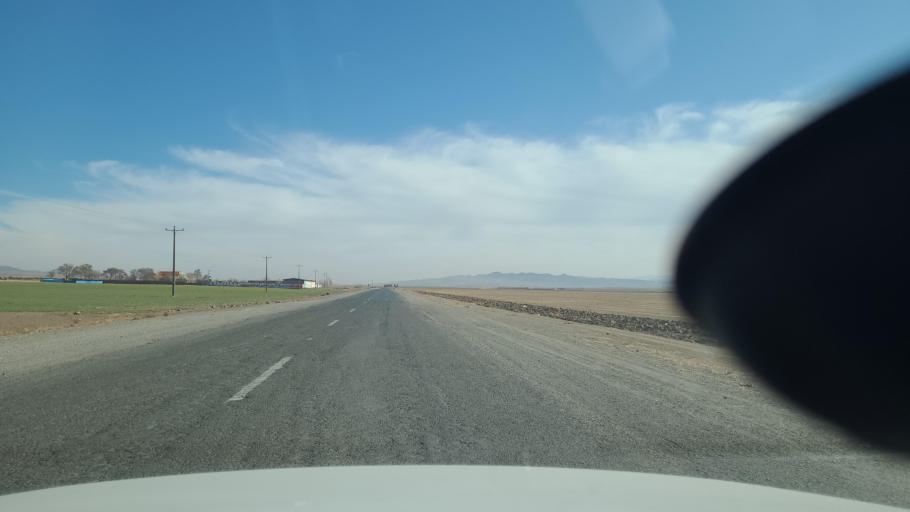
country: IR
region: Razavi Khorasan
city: Dowlatabad
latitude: 35.5999
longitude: 59.4669
